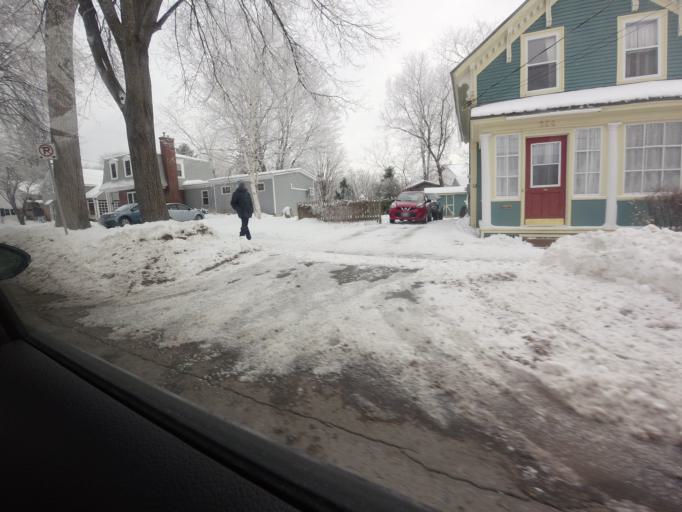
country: CA
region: New Brunswick
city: Fredericton
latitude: 45.9542
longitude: -66.6352
